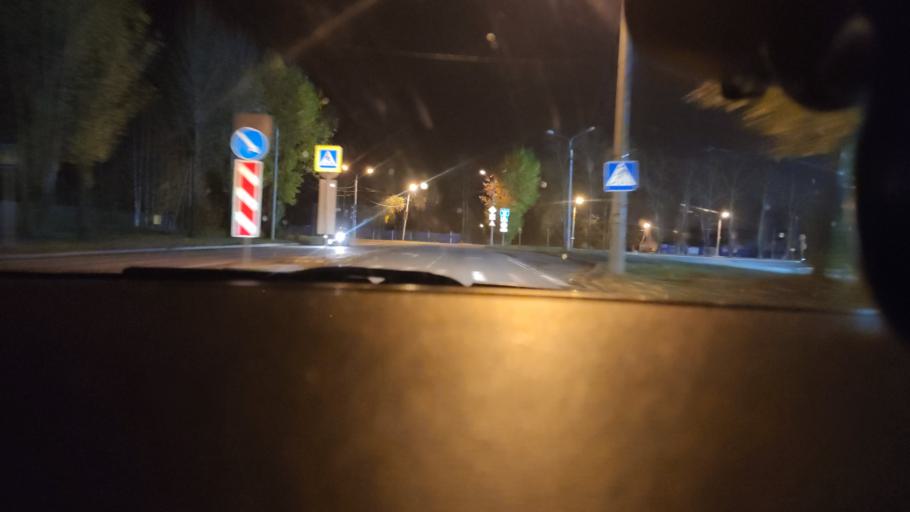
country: RU
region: Perm
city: Perm
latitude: 58.0511
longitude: 56.3534
